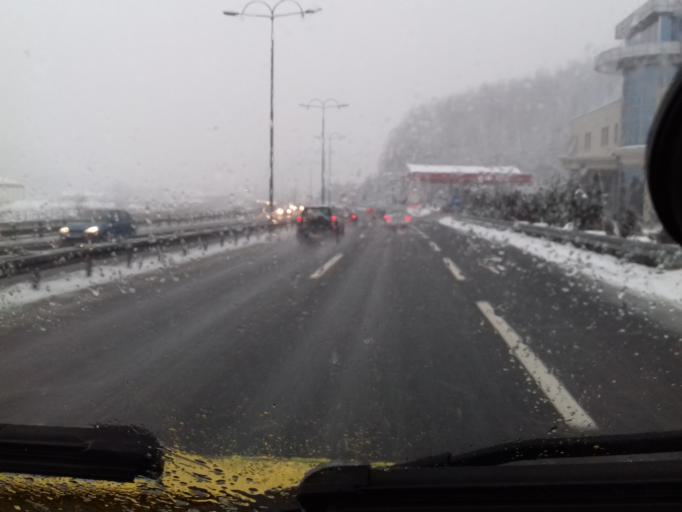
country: BA
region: Federation of Bosnia and Herzegovina
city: Hadzici
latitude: 43.8453
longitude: 18.2487
